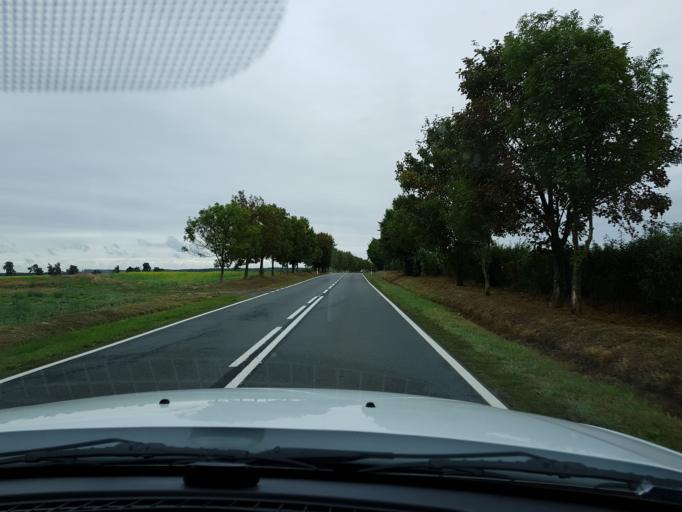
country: PL
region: West Pomeranian Voivodeship
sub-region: Powiat gryfinski
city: Chojna
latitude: 53.0154
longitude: 14.4370
